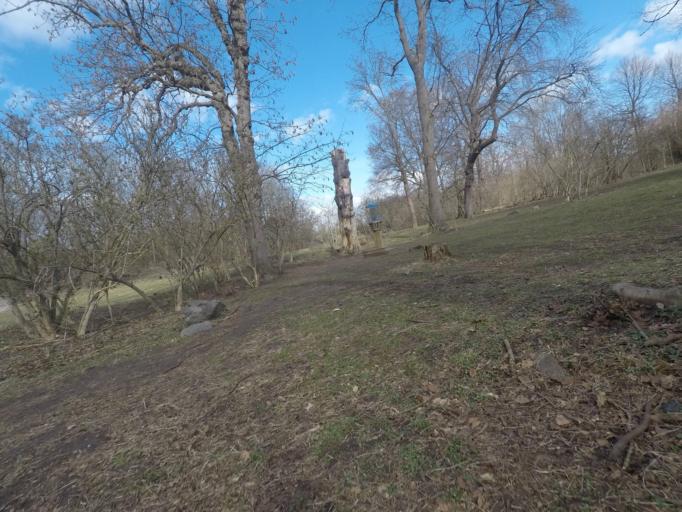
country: SE
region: Skane
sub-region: Burlovs Kommun
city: Arloev
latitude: 55.5968
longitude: 13.0701
